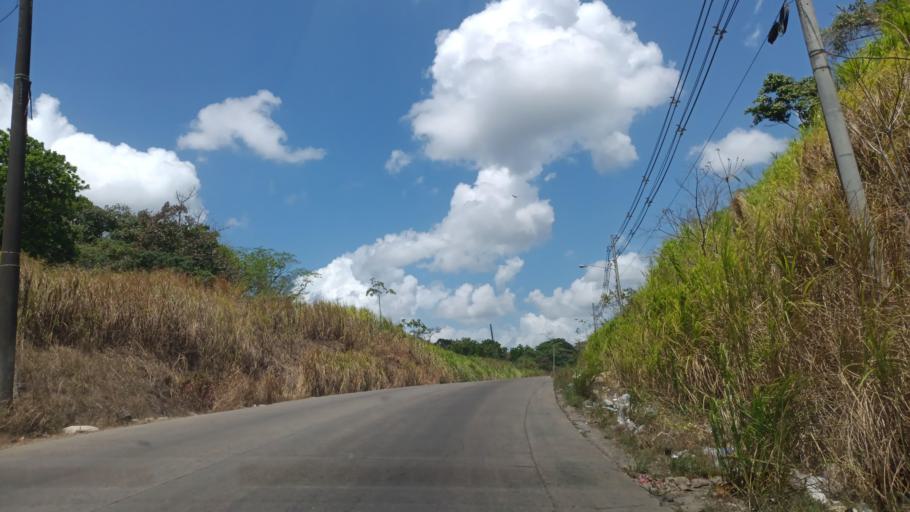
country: PA
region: Panama
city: Las Cumbres
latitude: 9.0420
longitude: -79.5625
